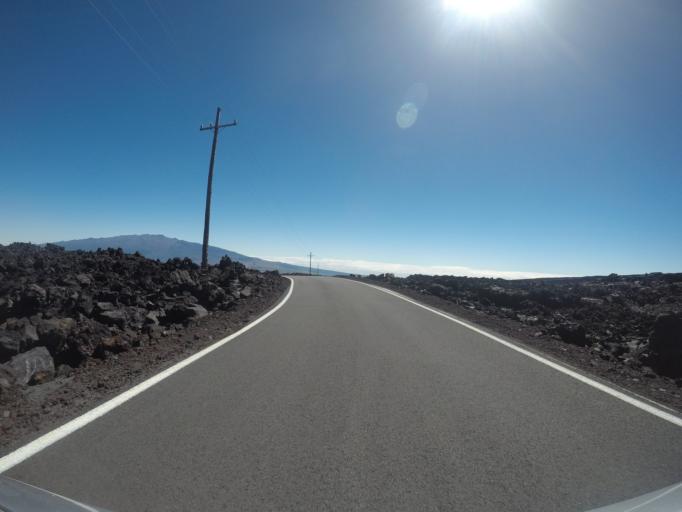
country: US
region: Hawaii
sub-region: Hawaii County
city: Volcano
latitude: 19.5569
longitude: -155.5340
